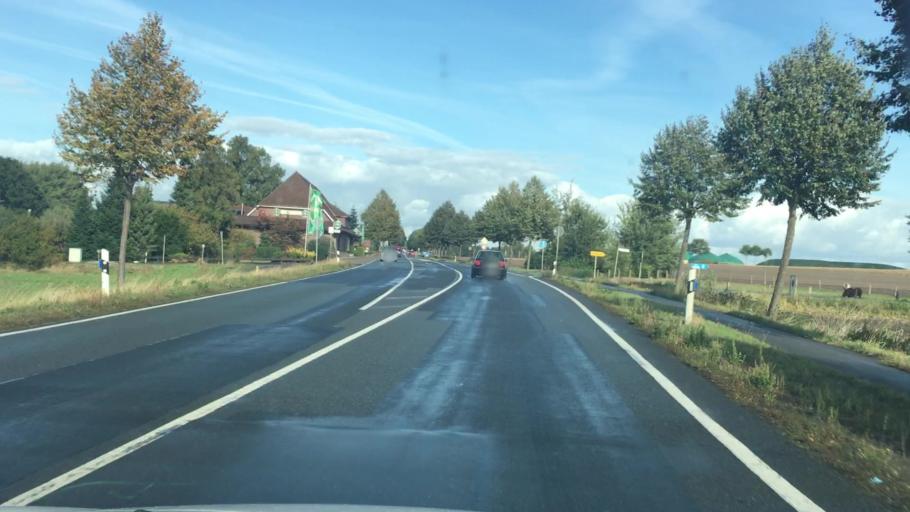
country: DE
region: Lower Saxony
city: Varrel
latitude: 52.6549
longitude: 8.7628
